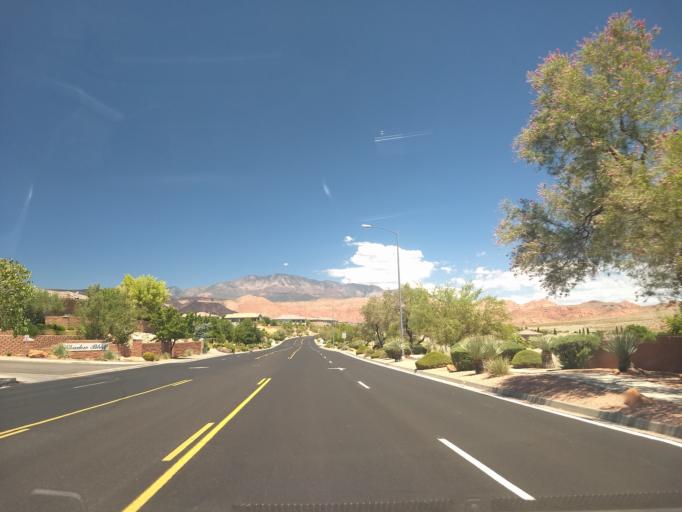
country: US
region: Utah
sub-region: Washington County
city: Washington
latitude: 37.1473
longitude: -113.5300
